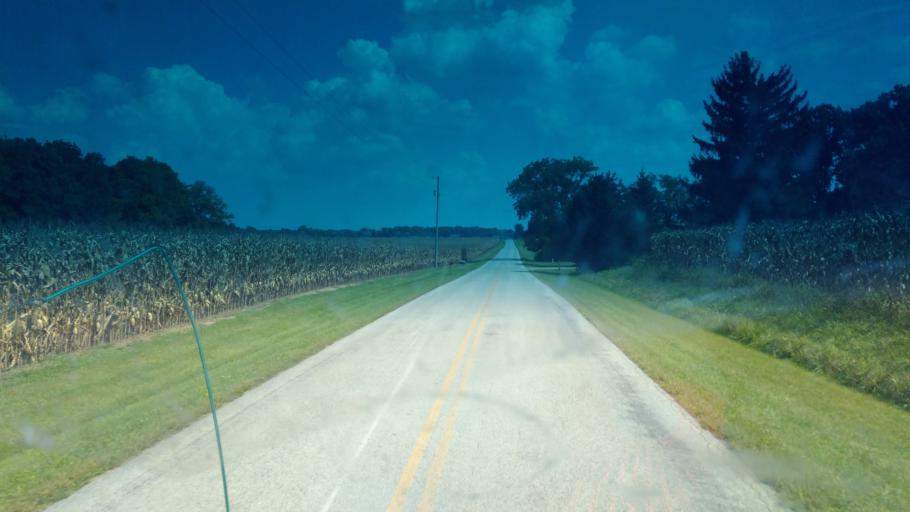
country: US
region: Ohio
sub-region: Hardin County
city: Ada
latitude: 40.7186
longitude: -83.8008
